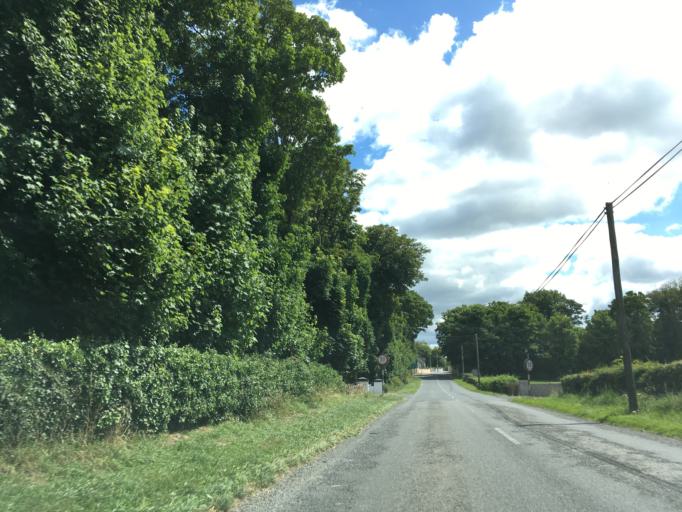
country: IE
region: Munster
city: Cashel
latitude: 52.4424
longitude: -7.8874
